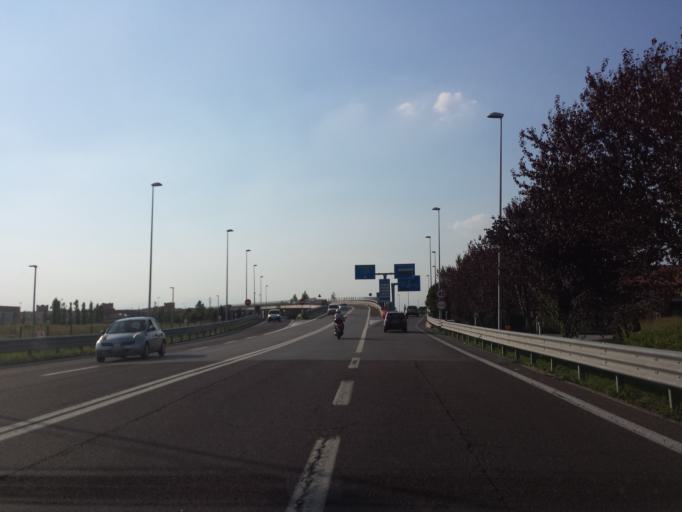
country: IT
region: Veneto
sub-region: Provincia di Vicenza
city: Torri di Quartesolo
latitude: 45.5115
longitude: 11.6286
